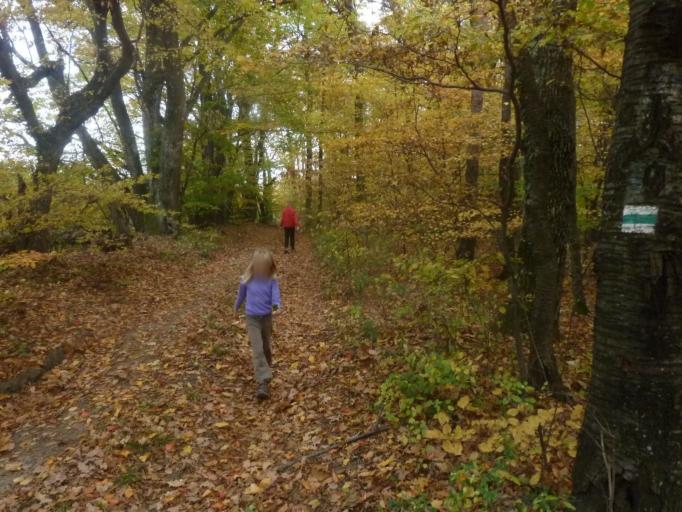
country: HU
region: Zala
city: Nagykanizsa
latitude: 46.5435
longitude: 17.0154
